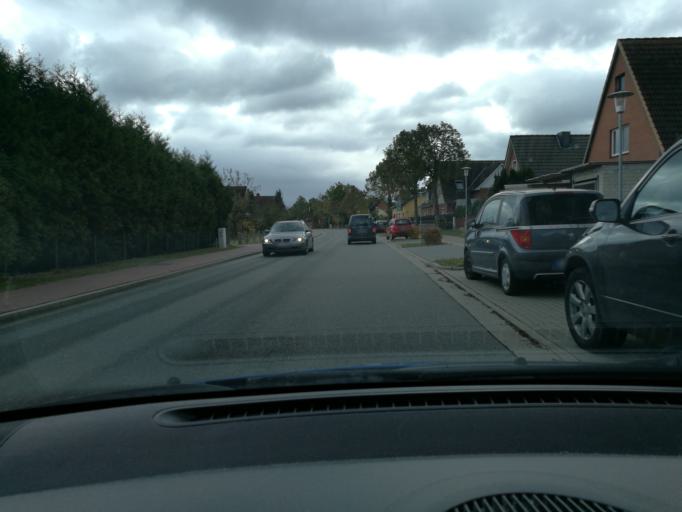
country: DE
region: Schleswig-Holstein
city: Pogeez
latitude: 53.7521
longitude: 10.7282
